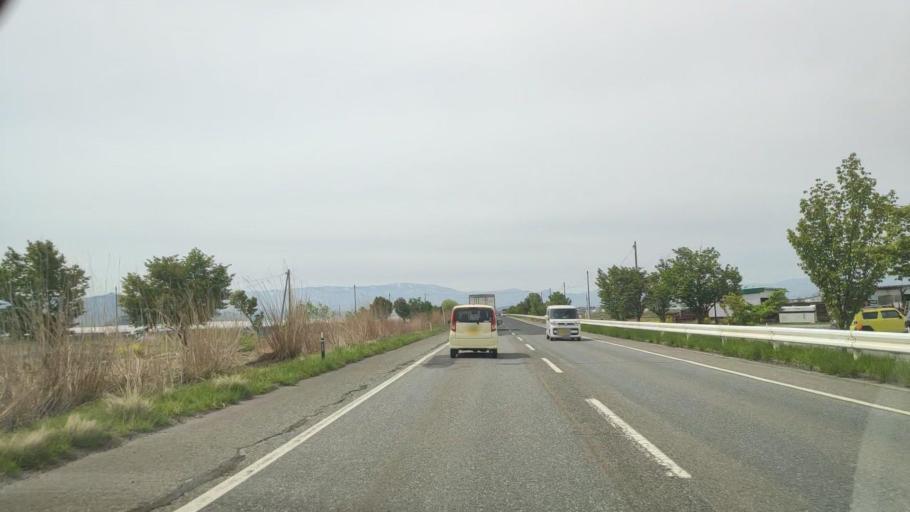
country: JP
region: Yamagata
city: Takahata
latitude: 38.0425
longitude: 140.1747
